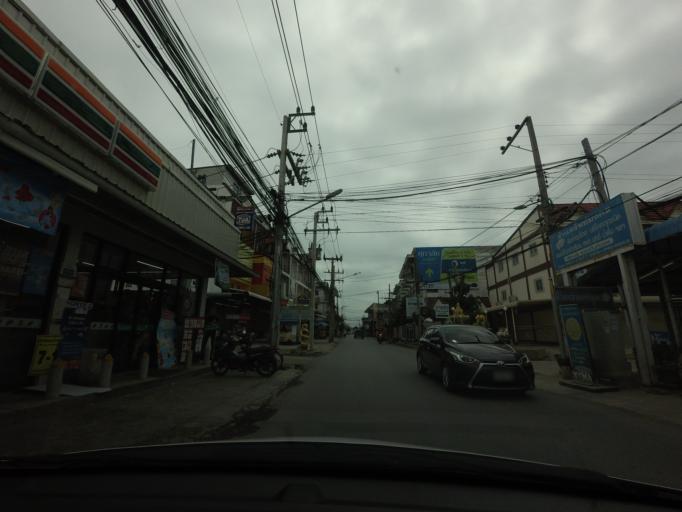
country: TH
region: Pathum Thani
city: Lam Luk Ka
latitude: 13.9313
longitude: 100.7504
